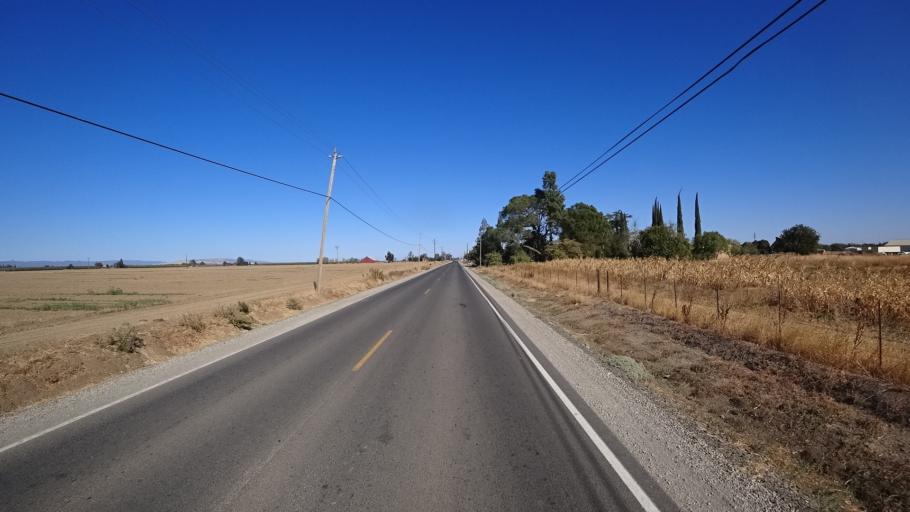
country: US
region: California
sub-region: Yolo County
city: Cottonwood
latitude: 38.6261
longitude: -121.9714
